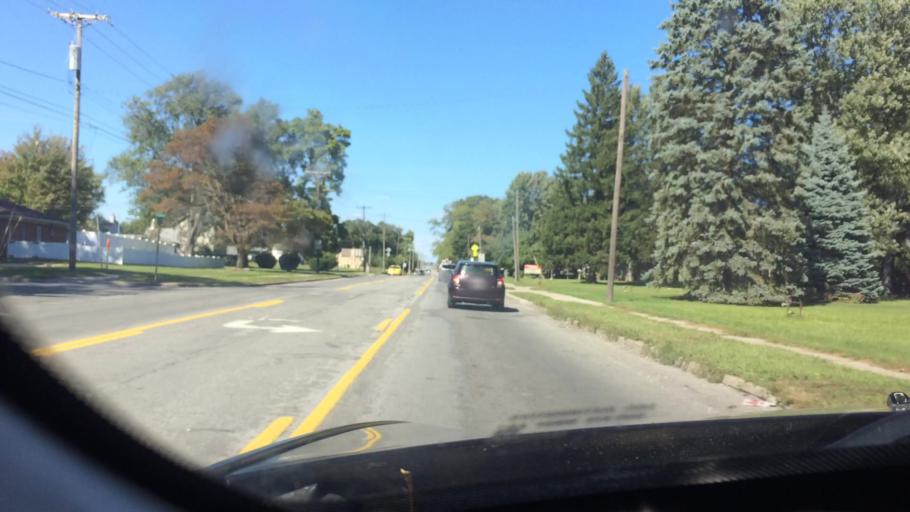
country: US
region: Ohio
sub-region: Lucas County
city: Ottawa Hills
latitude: 41.6636
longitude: -83.6825
